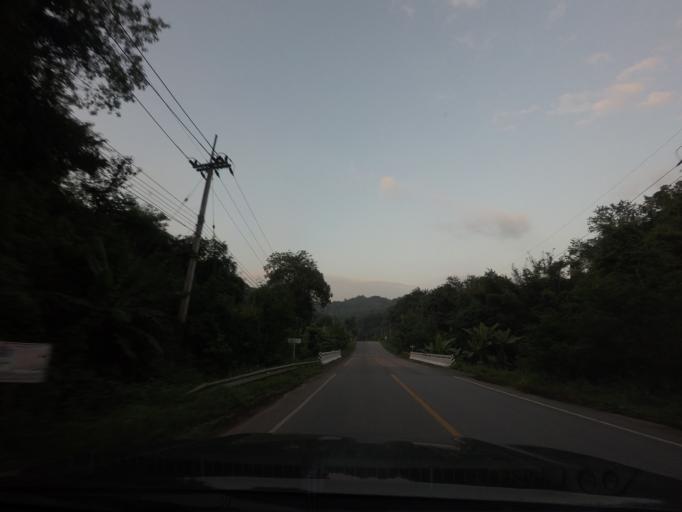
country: TH
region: Nan
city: Na Noi
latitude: 18.4146
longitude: 100.7022
